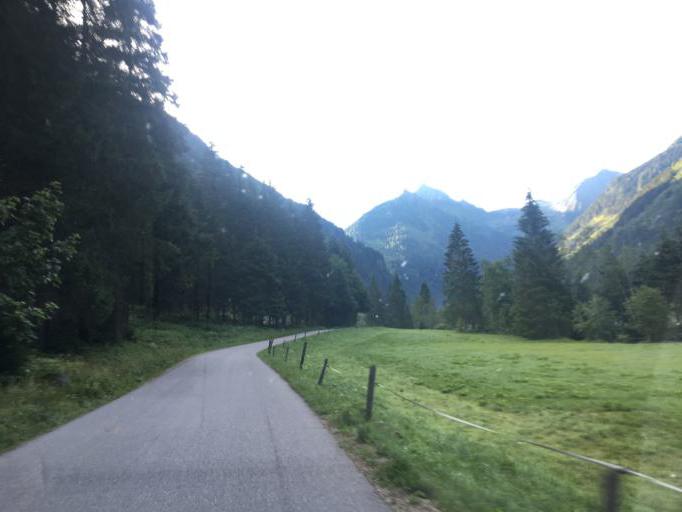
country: AT
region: Styria
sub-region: Politischer Bezirk Liezen
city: Schladming
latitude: 47.3426
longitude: 13.7334
